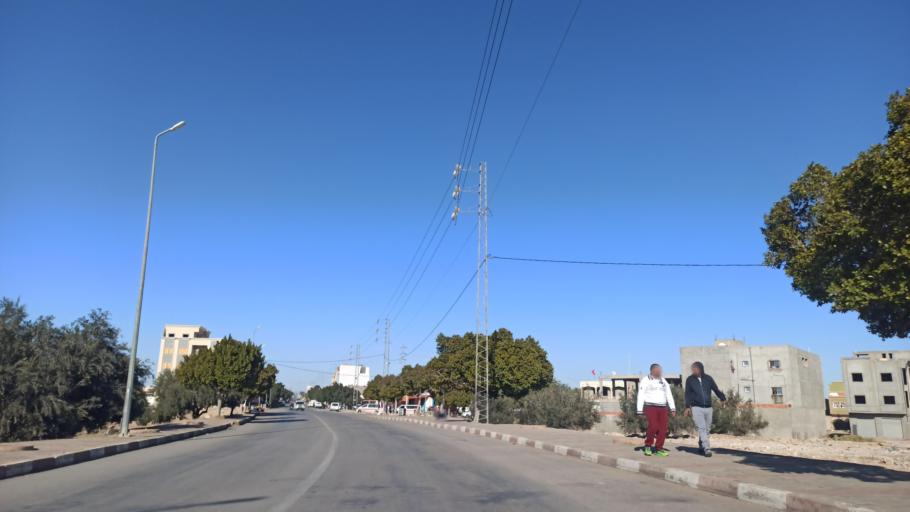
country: TN
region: Sidi Bu Zayd
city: Jilma
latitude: 35.2709
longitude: 9.4190
